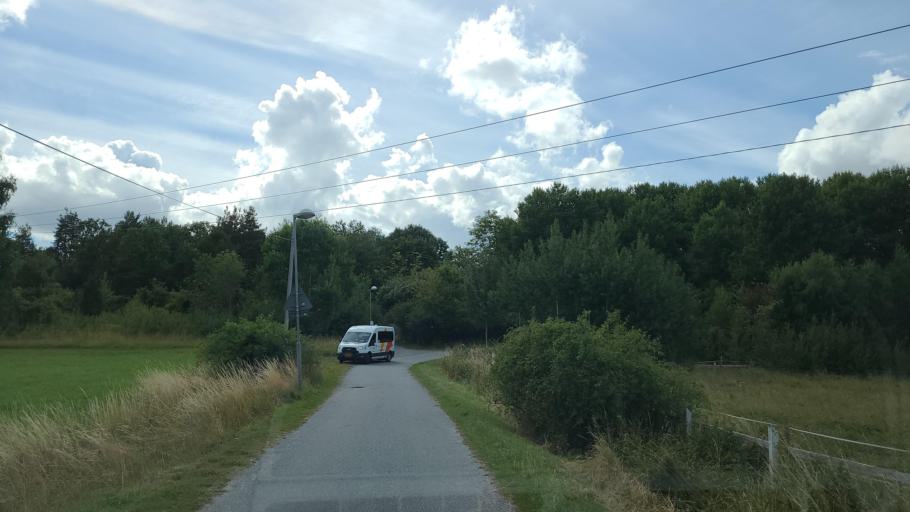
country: SE
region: Stockholm
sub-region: Stockholms Kommun
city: Kista
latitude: 59.3996
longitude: 17.9216
